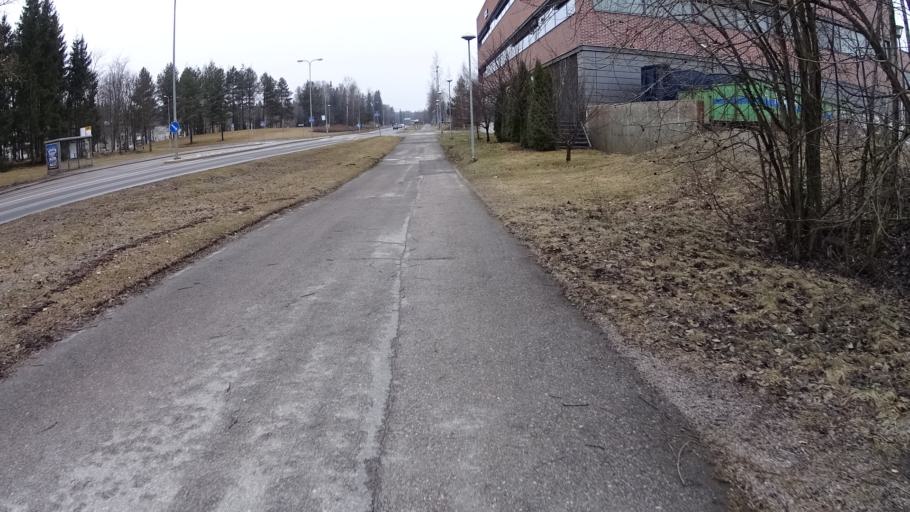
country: FI
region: Uusimaa
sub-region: Helsinki
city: Kilo
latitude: 60.2837
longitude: 24.8431
